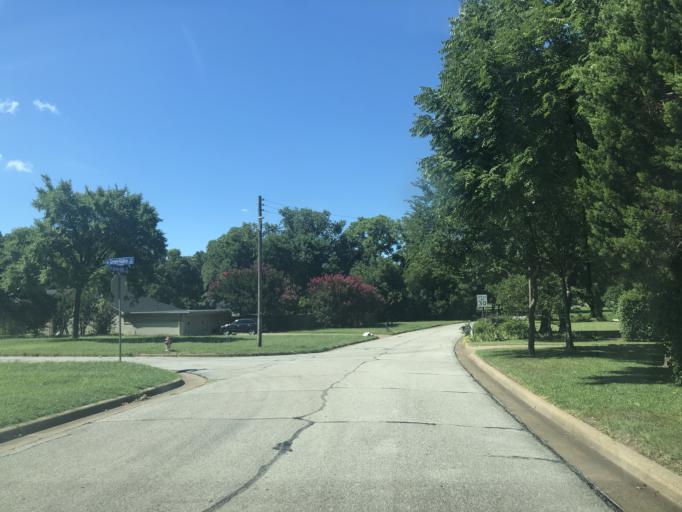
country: US
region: Texas
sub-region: Dallas County
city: Duncanville
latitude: 32.6405
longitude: -96.9383
